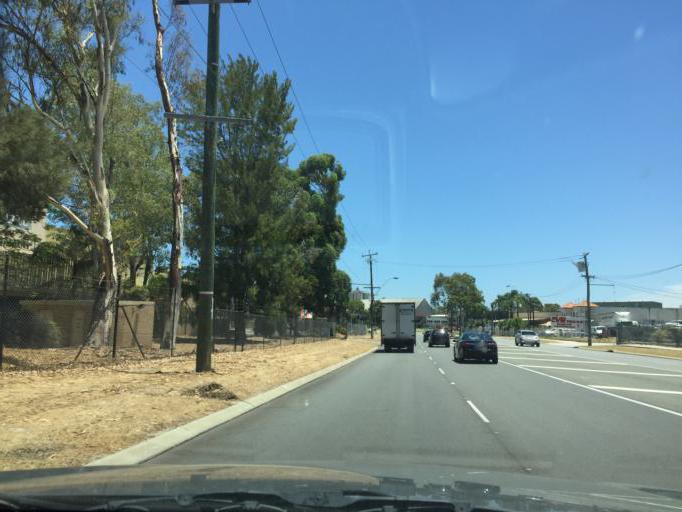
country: AU
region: Western Australia
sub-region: Canning
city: Canning Vale
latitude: -32.0598
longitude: 115.9209
